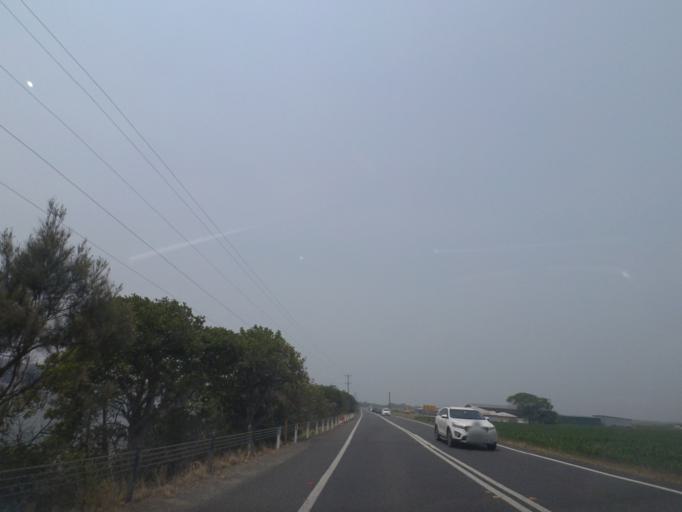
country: AU
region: New South Wales
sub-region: Richmond Valley
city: Evans Head
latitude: -28.9955
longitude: 153.4559
